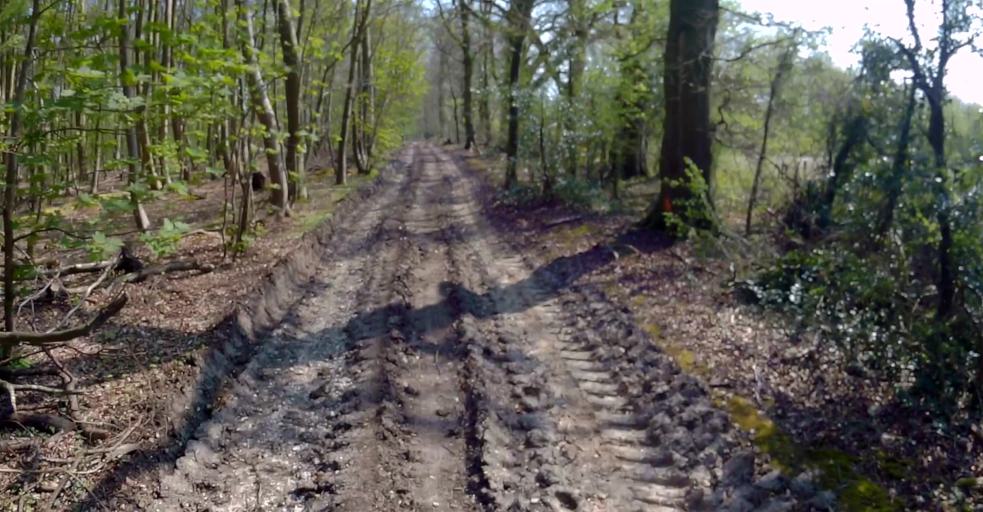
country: GB
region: England
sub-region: Hampshire
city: Overton
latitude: 51.1826
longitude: -1.2423
